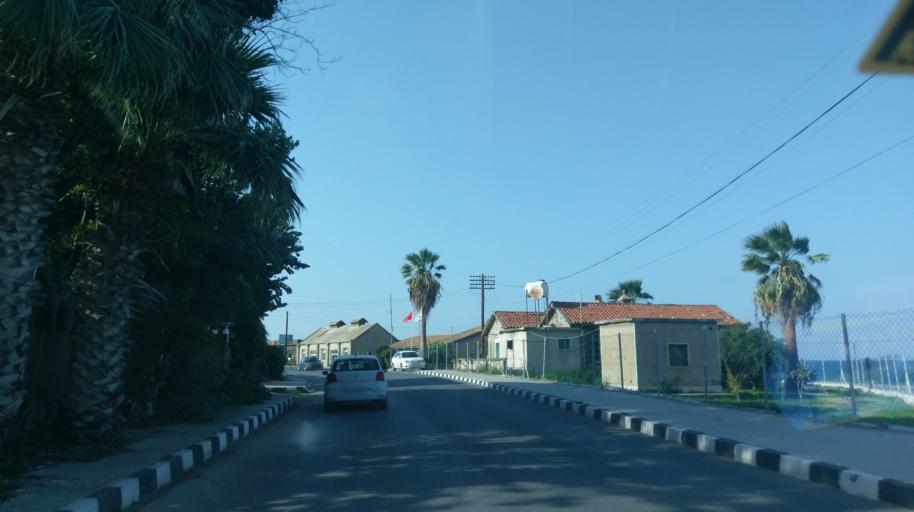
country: CY
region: Lefkosia
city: Lefka
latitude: 35.1415
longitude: 32.8230
